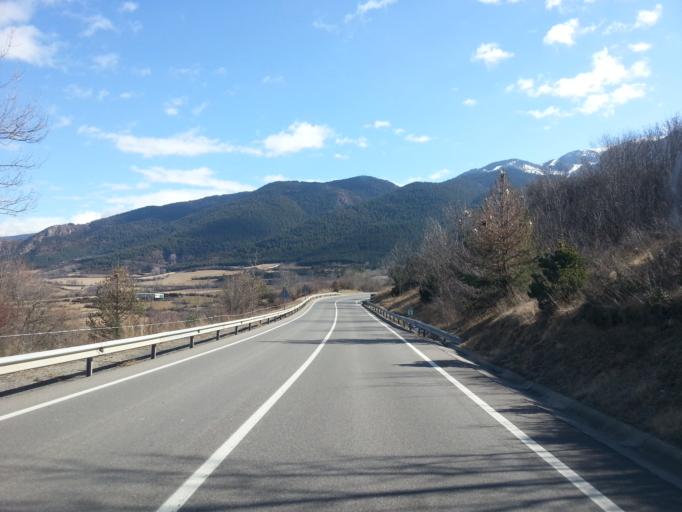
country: ES
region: Catalonia
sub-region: Provincia de Girona
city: Urus
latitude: 42.3554
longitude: 1.8506
